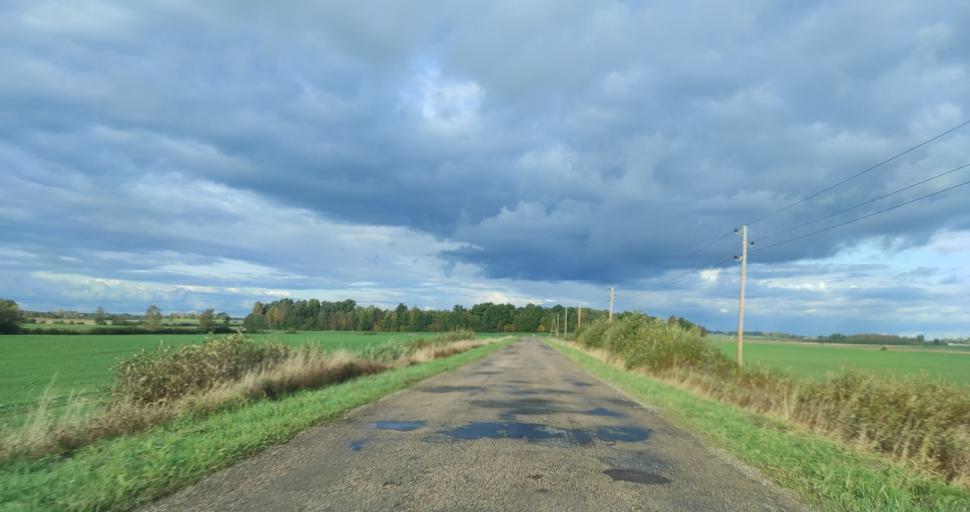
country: LV
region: Aizpute
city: Aizpute
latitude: 56.8026
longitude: 21.7160
